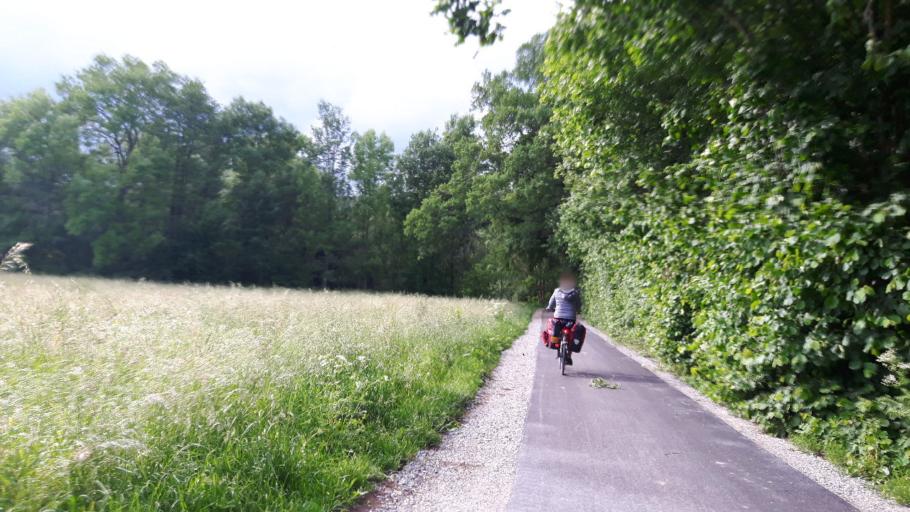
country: DE
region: Thuringia
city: Kranichfeld
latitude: 50.8575
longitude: 11.2412
